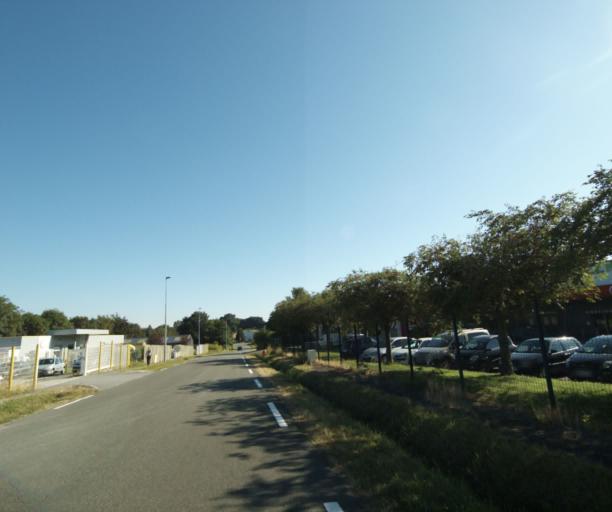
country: FR
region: Pays de la Loire
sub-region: Departement de la Mayenne
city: Laval
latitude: 48.0586
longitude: -0.7383
